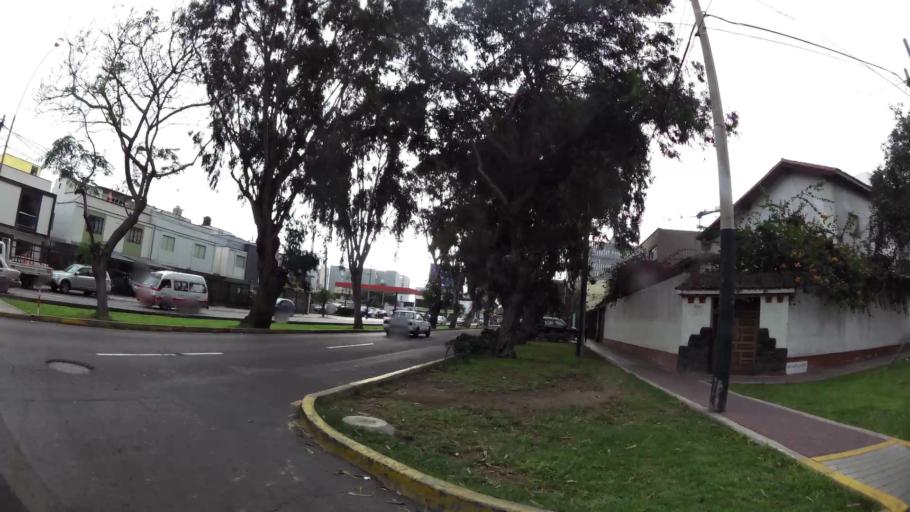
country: PE
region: Lima
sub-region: Lima
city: San Isidro
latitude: -12.1037
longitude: -77.0575
